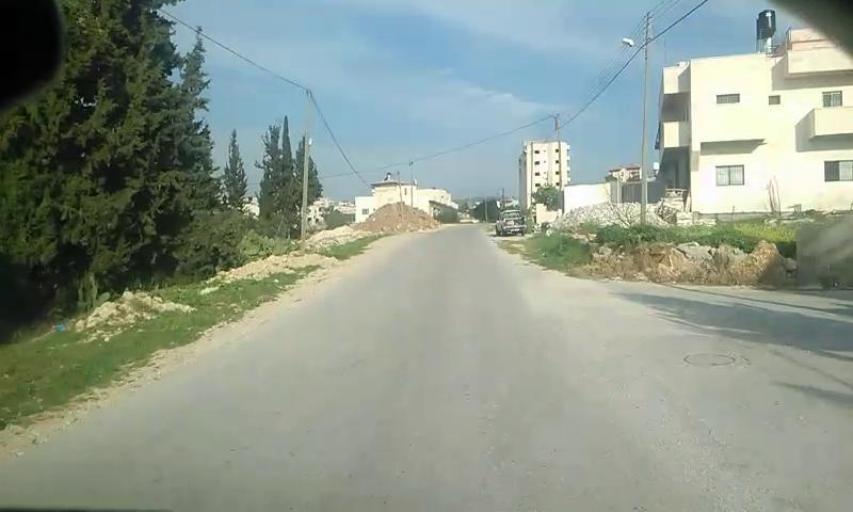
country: PS
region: West Bank
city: Nuba
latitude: 31.6140
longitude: 35.0265
